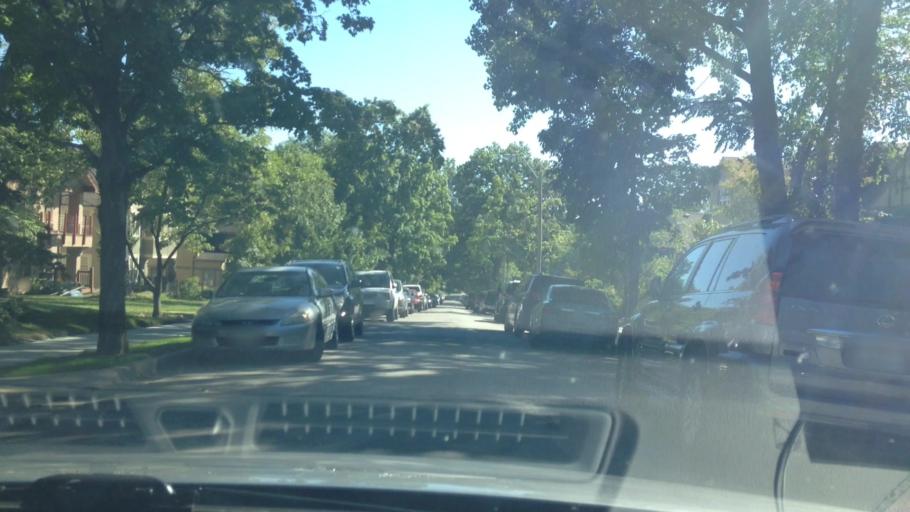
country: US
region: Kansas
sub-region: Johnson County
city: Westwood
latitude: 39.0406
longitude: -94.6010
